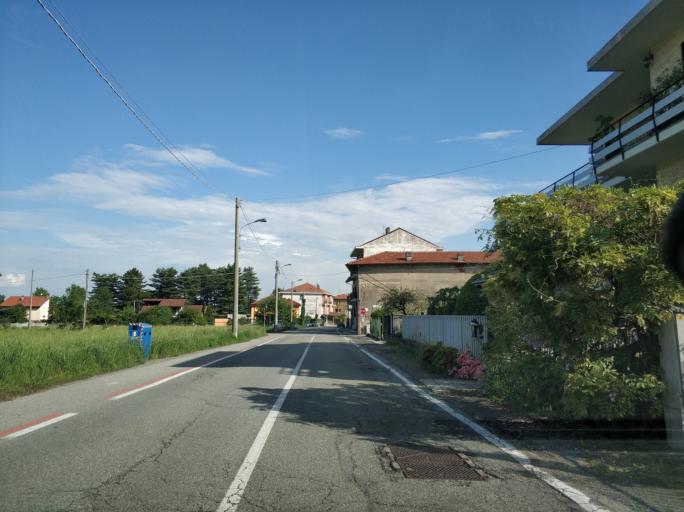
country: IT
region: Piedmont
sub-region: Provincia di Torino
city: Cafasse
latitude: 45.2522
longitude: 7.5123
